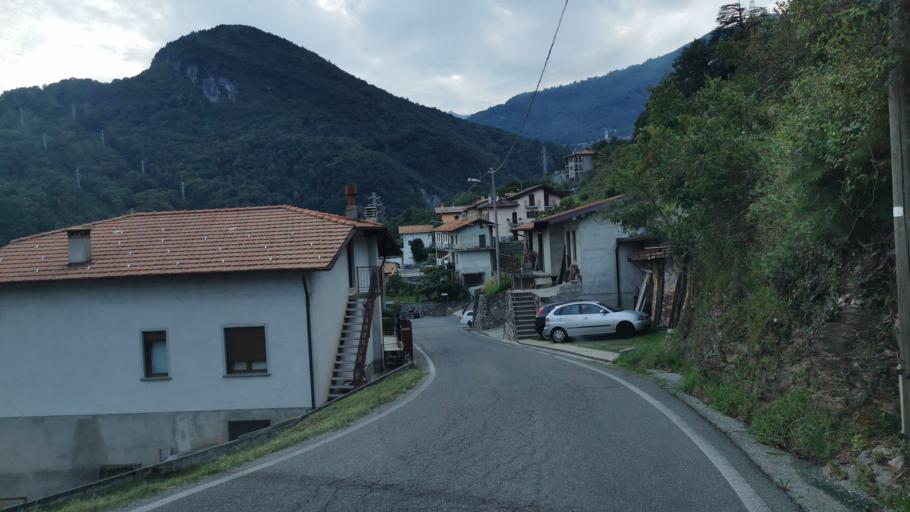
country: IT
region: Lombardy
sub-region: Provincia di Como
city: Vercana
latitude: 46.1609
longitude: 9.3319
